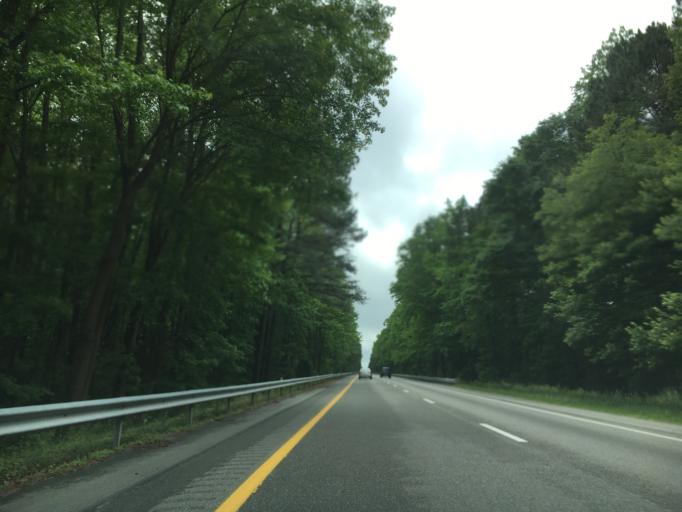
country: US
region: Virginia
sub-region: Brunswick County
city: Lawrenceville
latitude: 36.8585
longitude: -77.8496
